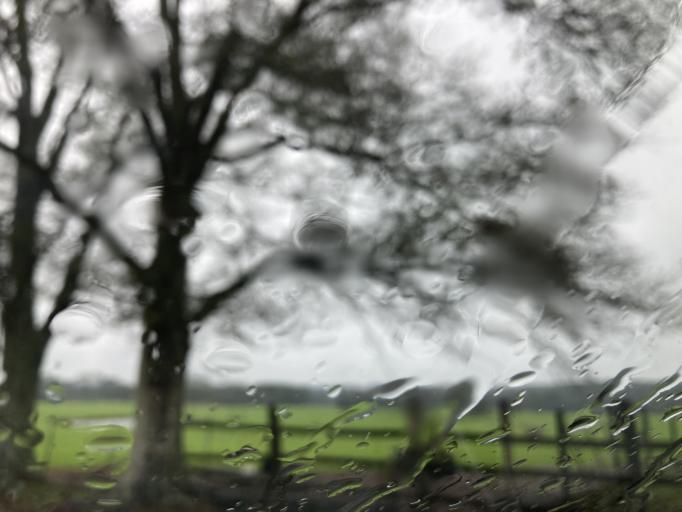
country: US
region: Mississippi
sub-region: Forrest County
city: Rawls Springs
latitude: 31.4857
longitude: -89.3823
